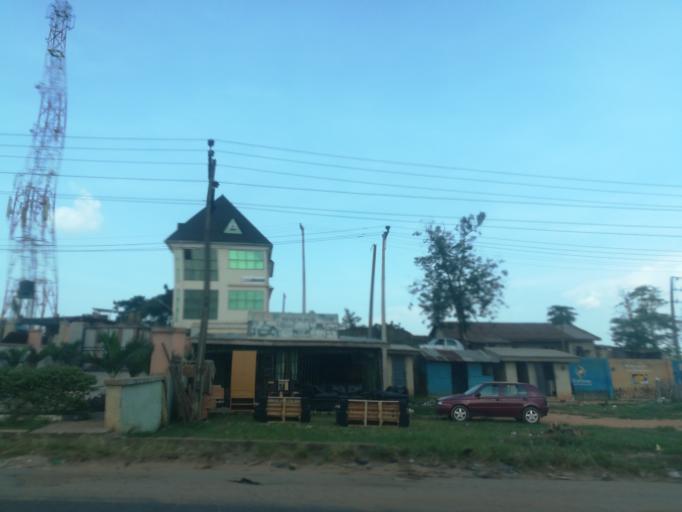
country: NG
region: Oyo
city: Ibadan
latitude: 7.4213
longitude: 3.9384
